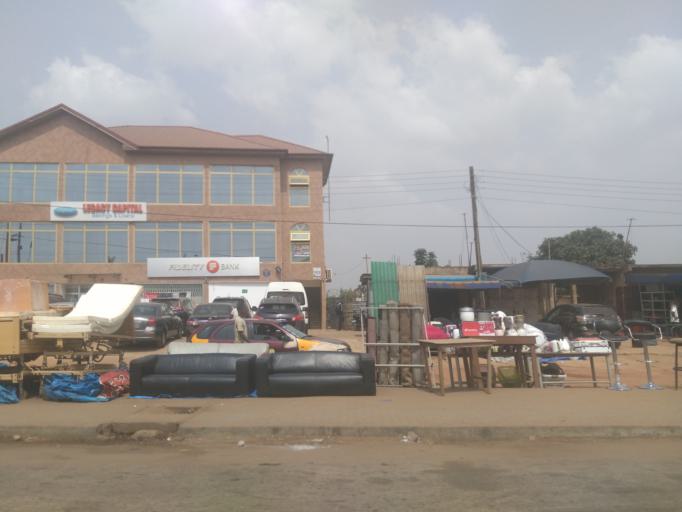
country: GH
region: Greater Accra
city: Dome
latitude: 5.6046
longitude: -0.2540
